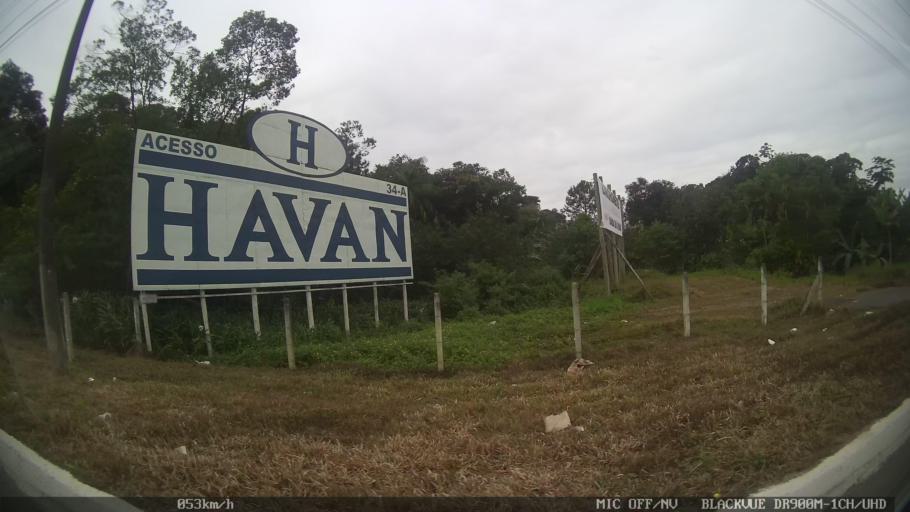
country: BR
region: Santa Catarina
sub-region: Joinville
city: Joinville
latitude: -26.2935
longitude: -48.8842
